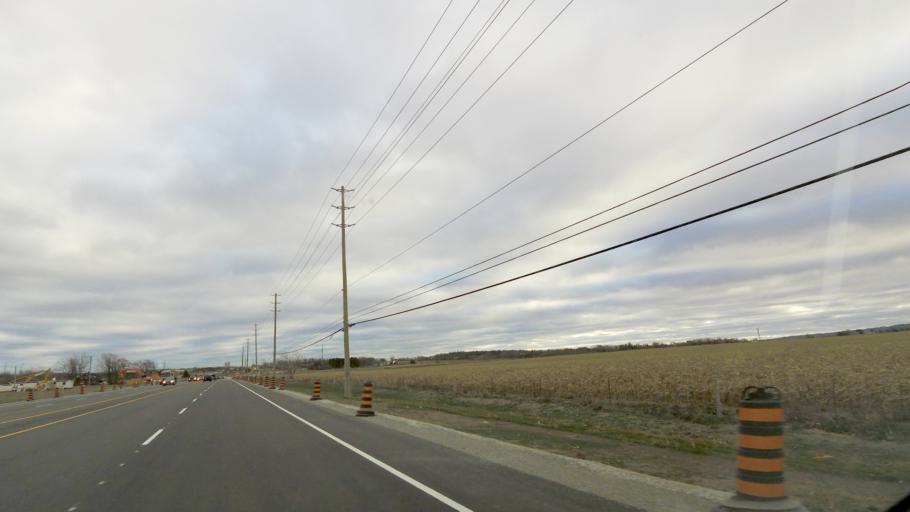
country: CA
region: Ontario
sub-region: Halton
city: Milton
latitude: 43.4711
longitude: -79.8131
